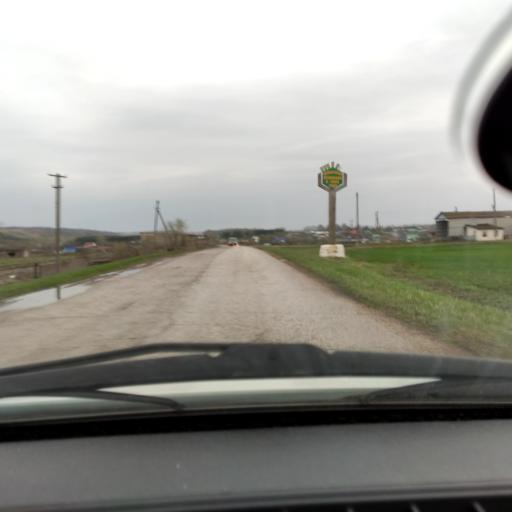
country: RU
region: Bashkortostan
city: Tolbazy
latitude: 54.1691
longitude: 55.9431
